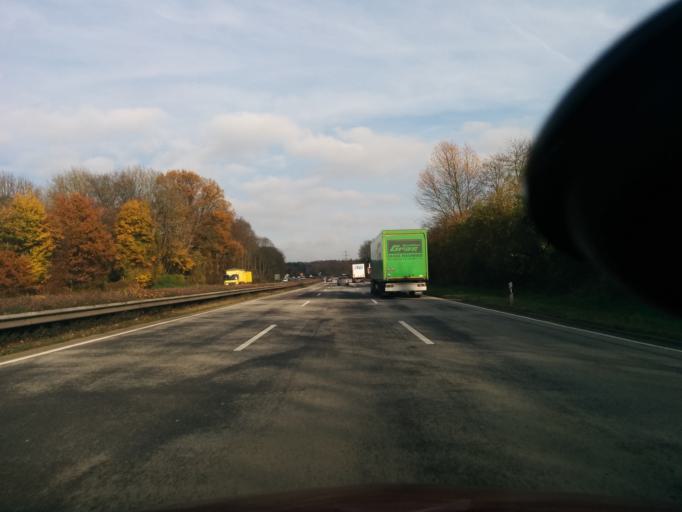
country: DE
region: Rheinland-Pfalz
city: Weitersburg
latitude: 50.4272
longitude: 7.6259
